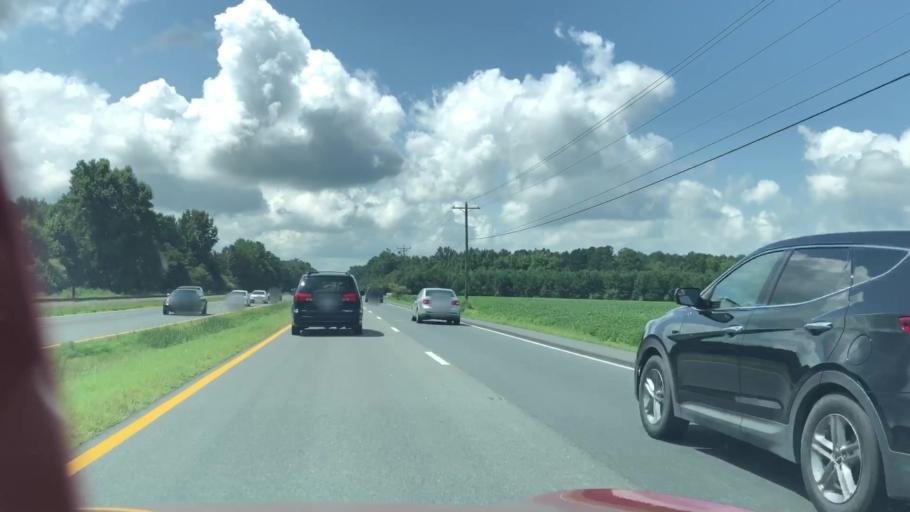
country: US
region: Virginia
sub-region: Accomack County
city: Onancock
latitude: 37.6630
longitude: -75.7340
